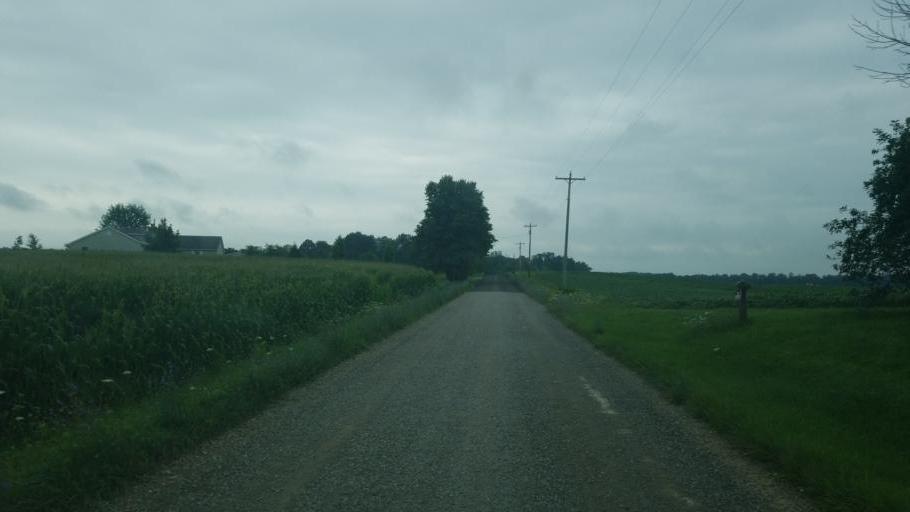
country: US
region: Ohio
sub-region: Knox County
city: Centerburg
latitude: 40.3859
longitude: -82.7419
